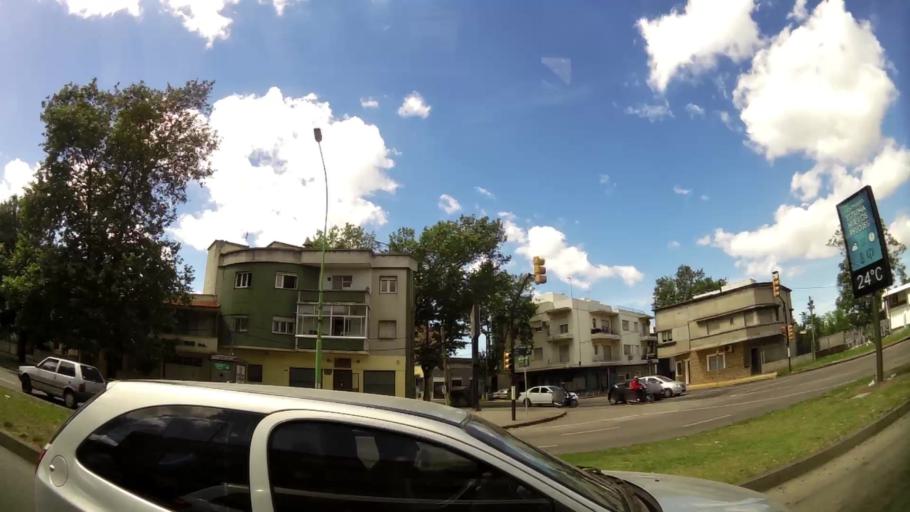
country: UY
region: Montevideo
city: Montevideo
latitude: -34.8729
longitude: -56.2050
